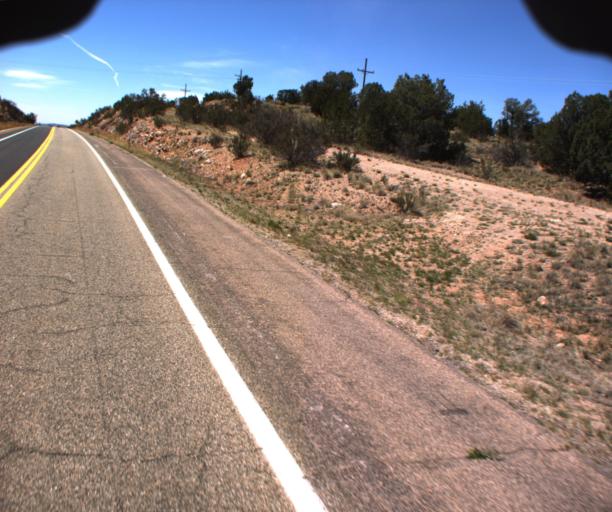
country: US
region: Arizona
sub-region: Mohave County
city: Peach Springs
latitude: 35.5261
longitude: -113.2168
